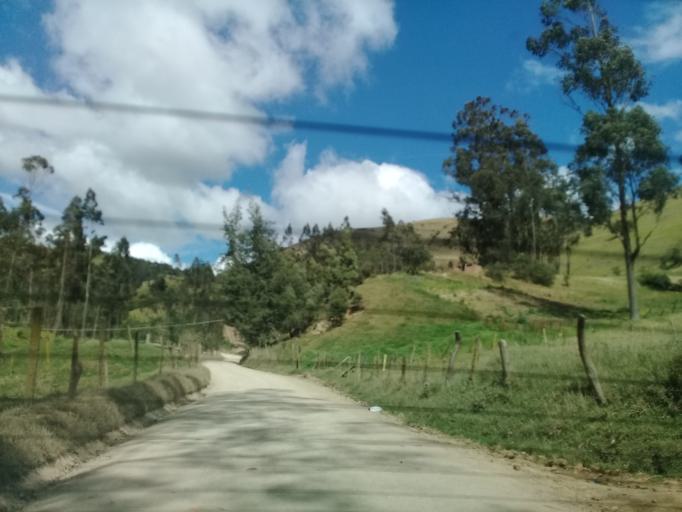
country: CO
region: Cundinamarca
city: Choconta
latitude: 5.1558
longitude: -73.7072
